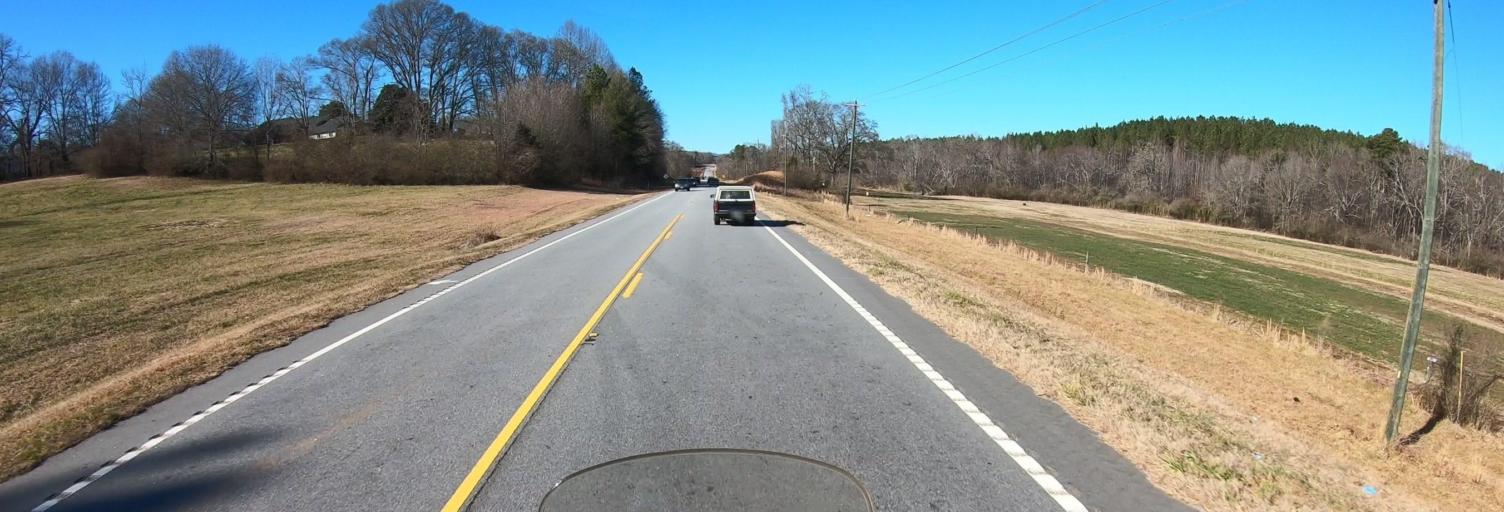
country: US
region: South Carolina
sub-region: Oconee County
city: Walhalla
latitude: 34.7886
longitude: -83.0272
